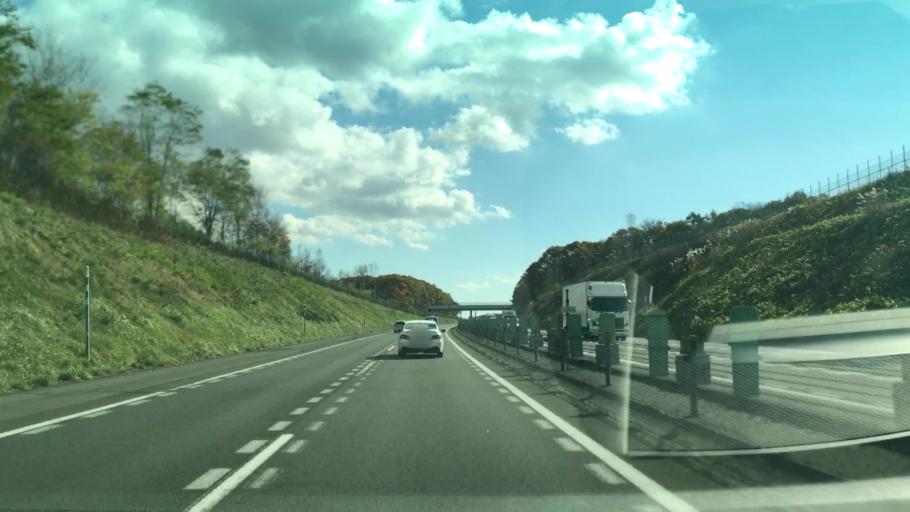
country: JP
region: Hokkaido
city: Kitahiroshima
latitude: 42.9210
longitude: 141.5438
